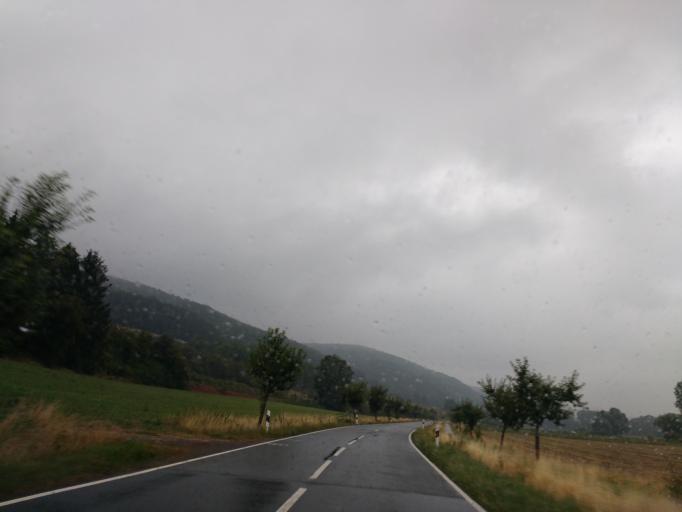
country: DE
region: Lower Saxony
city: Bad Pyrmont
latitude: 51.9833
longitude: 9.2953
